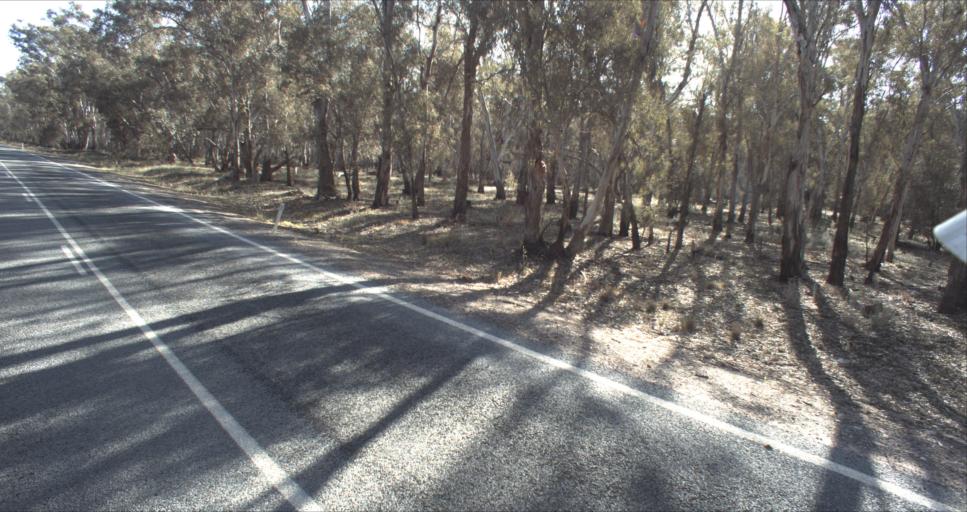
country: AU
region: New South Wales
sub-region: Leeton
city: Leeton
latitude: -34.6255
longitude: 146.3798
